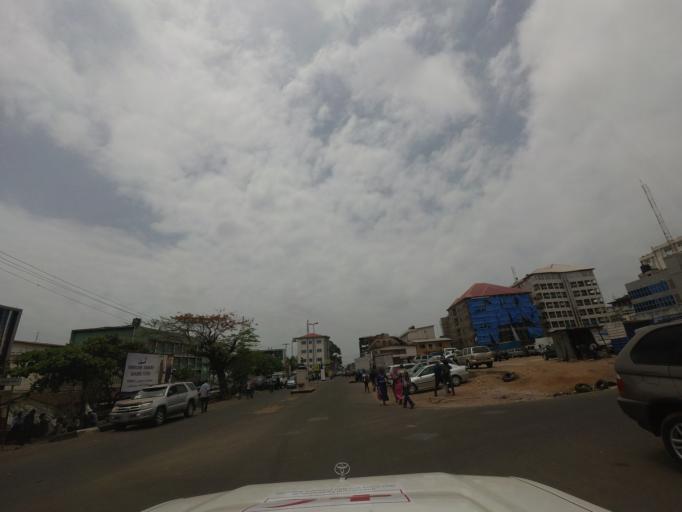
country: SL
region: Western Area
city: Freetown
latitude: 8.4903
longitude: -13.2356
